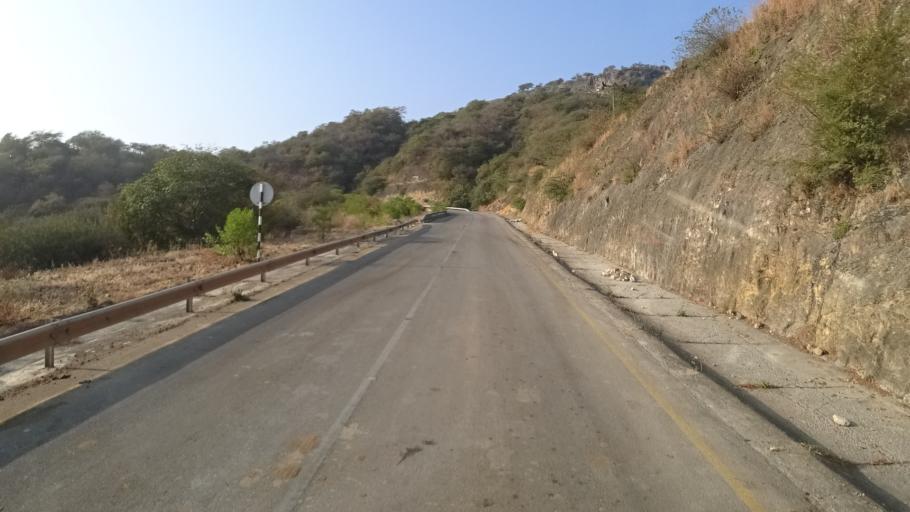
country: YE
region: Al Mahrah
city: Hawf
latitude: 16.7617
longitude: 53.3393
